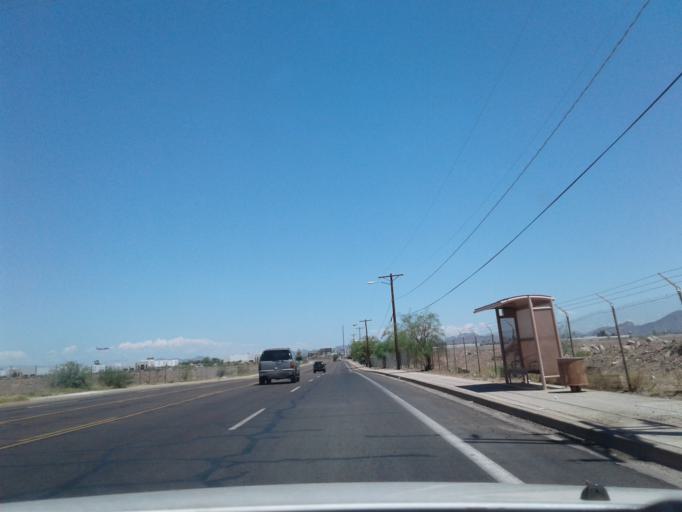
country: US
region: Arizona
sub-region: Maricopa County
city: Phoenix
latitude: 33.4106
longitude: -112.0297
